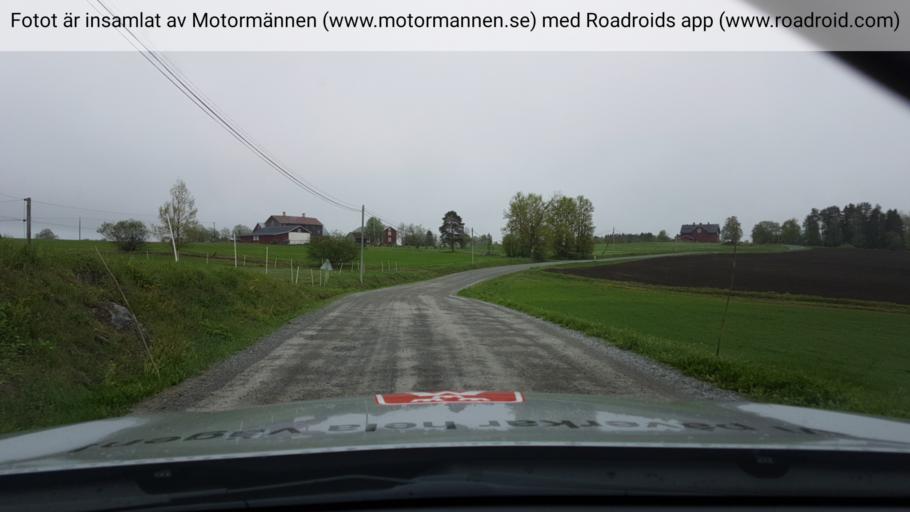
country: SE
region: Jaemtland
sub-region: Bergs Kommun
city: Hoverberg
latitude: 63.0062
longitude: 14.3877
